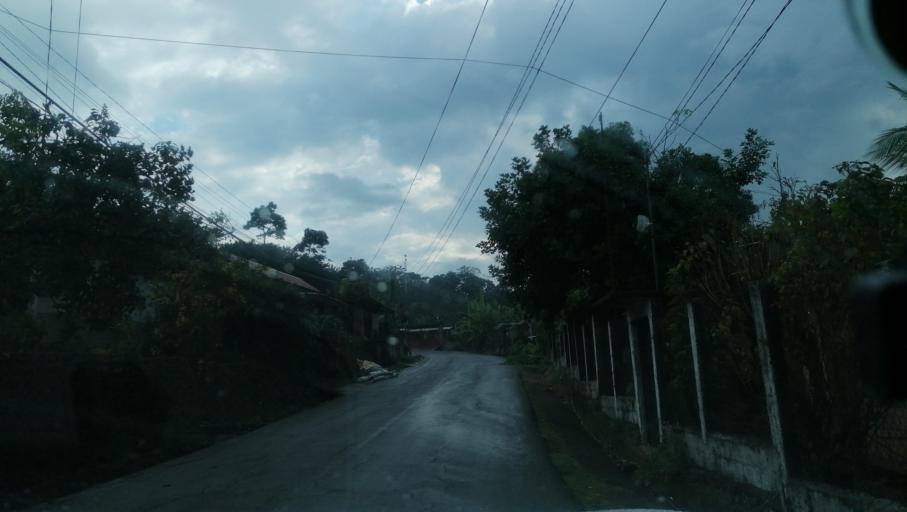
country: MX
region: Chiapas
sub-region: Cacahoatan
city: Benito Juarez
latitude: 15.0491
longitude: -92.1892
